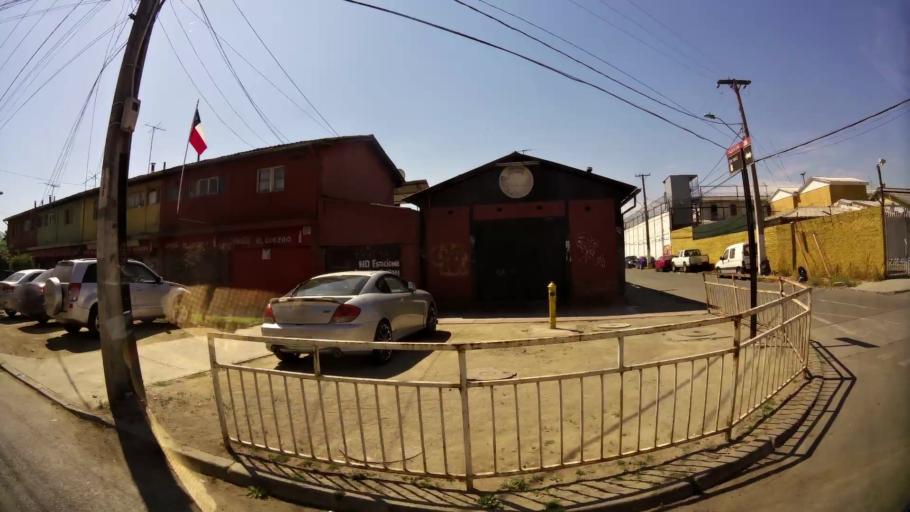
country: CL
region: Santiago Metropolitan
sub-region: Provincia de Talagante
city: Talagante
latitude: -33.6555
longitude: -70.9248
